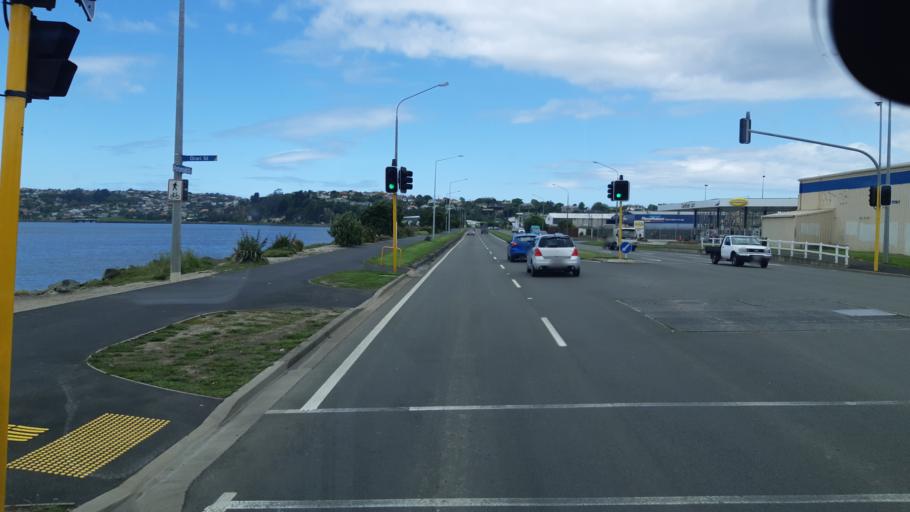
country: NZ
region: Otago
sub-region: Dunedin City
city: Dunedin
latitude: -45.8876
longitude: 170.5076
